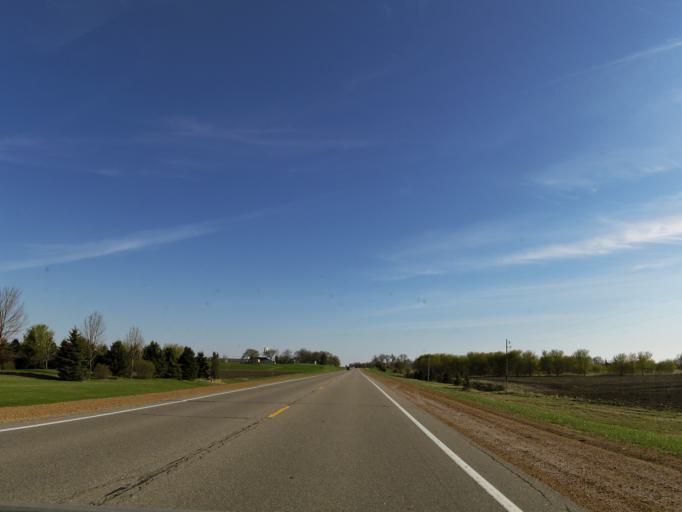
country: US
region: Minnesota
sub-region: Scott County
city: Prior Lake
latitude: 44.6443
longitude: -93.5012
